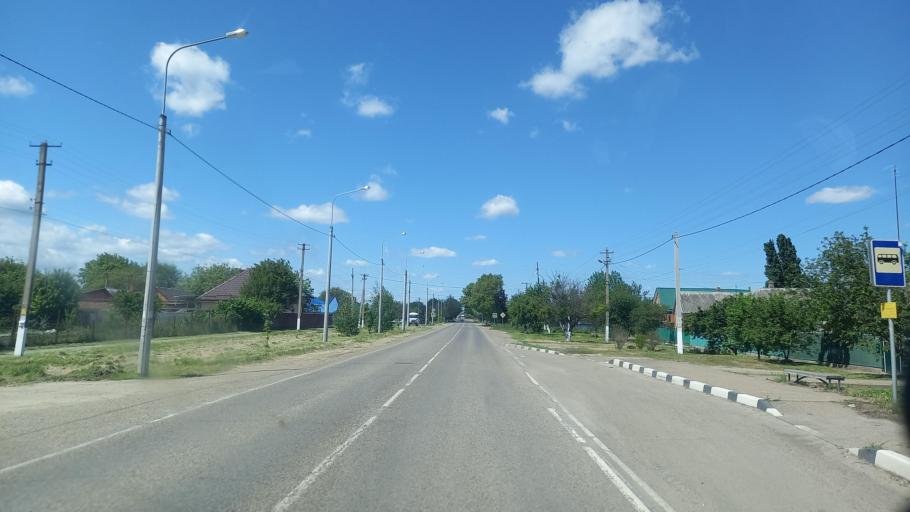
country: RU
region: Krasnodarskiy
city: Novoukrainskoye
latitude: 45.3805
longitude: 40.5072
